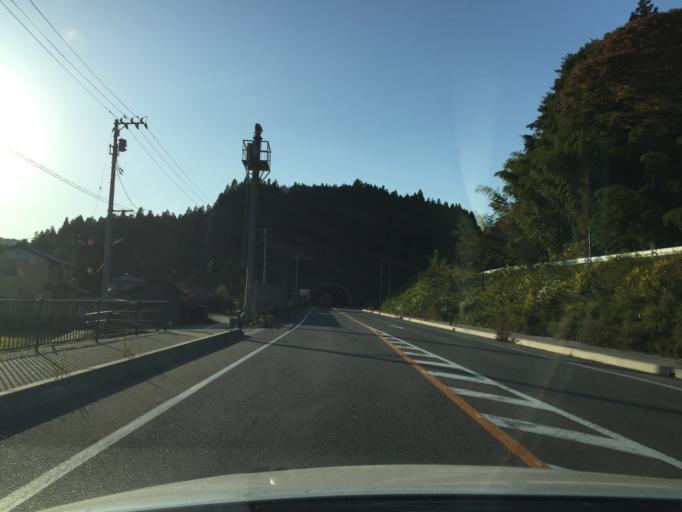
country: JP
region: Fukushima
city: Iwaki
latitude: 37.1257
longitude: 140.7294
